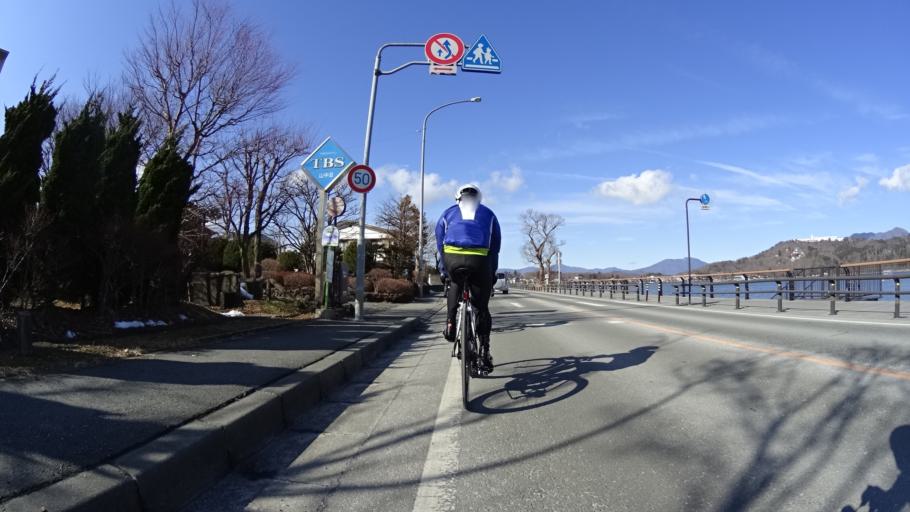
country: JP
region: Shizuoka
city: Gotemba
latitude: 35.4195
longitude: 138.8542
